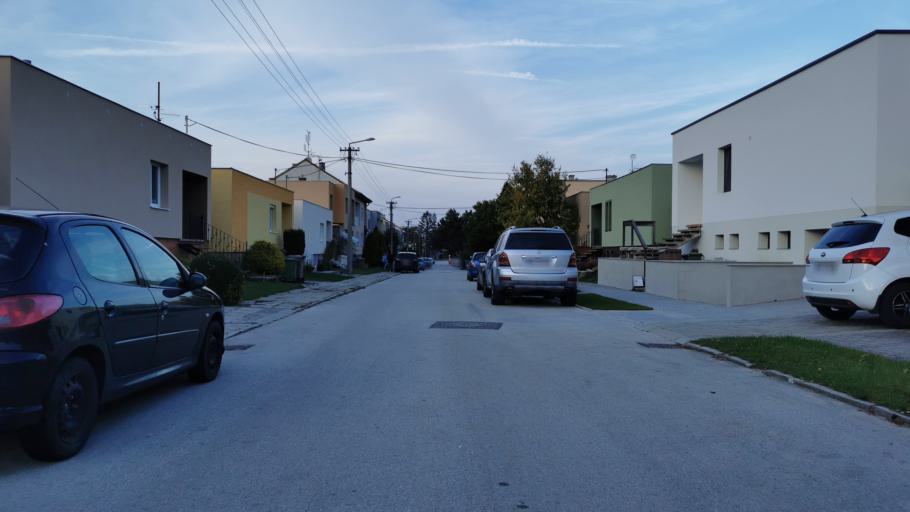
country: SK
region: Trnavsky
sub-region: Okres Skalica
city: Skalica
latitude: 48.8397
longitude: 17.2349
